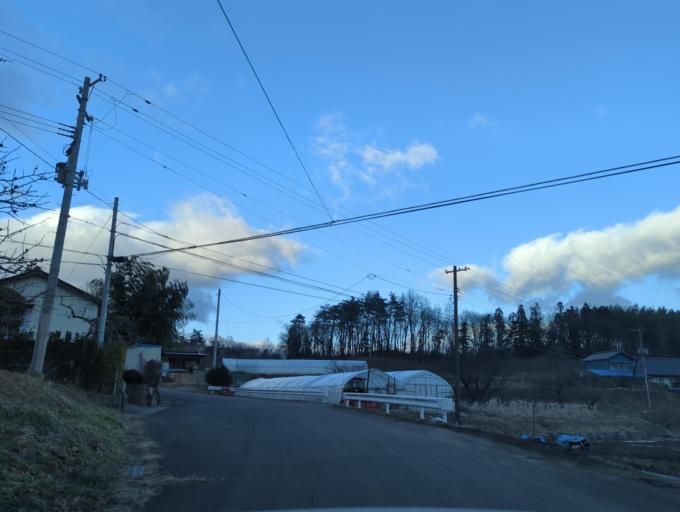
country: JP
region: Fukushima
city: Koriyama
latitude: 37.4323
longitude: 140.4043
